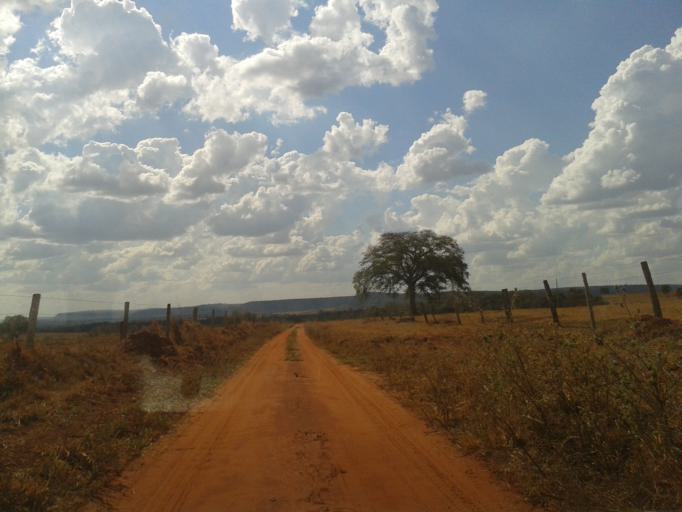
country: BR
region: Minas Gerais
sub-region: Santa Vitoria
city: Santa Vitoria
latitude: -19.2072
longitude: -49.9684
